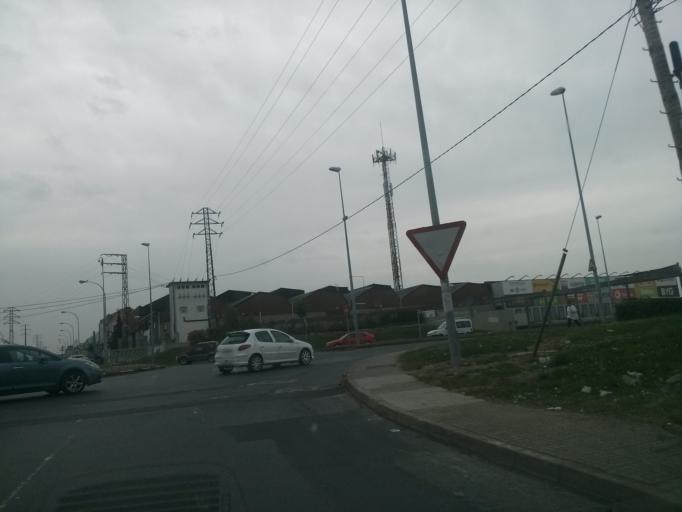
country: ES
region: Galicia
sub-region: Provincia de Lugo
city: Lugo
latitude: 43.0468
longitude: -7.5681
